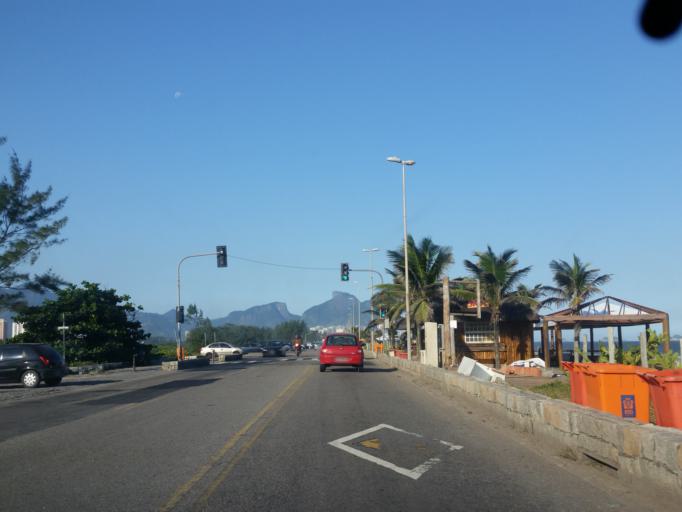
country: BR
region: Rio de Janeiro
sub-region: Nilopolis
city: Nilopolis
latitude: -23.0139
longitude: -43.4000
